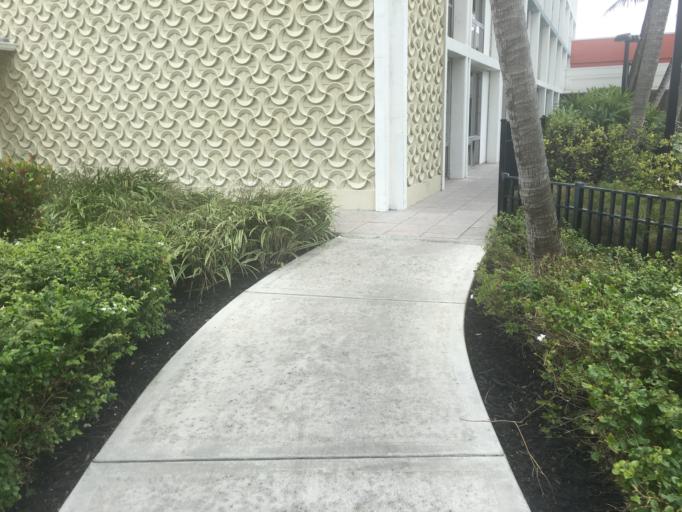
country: US
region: Florida
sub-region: Miami-Dade County
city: West Miami
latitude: 25.7845
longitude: -80.2625
